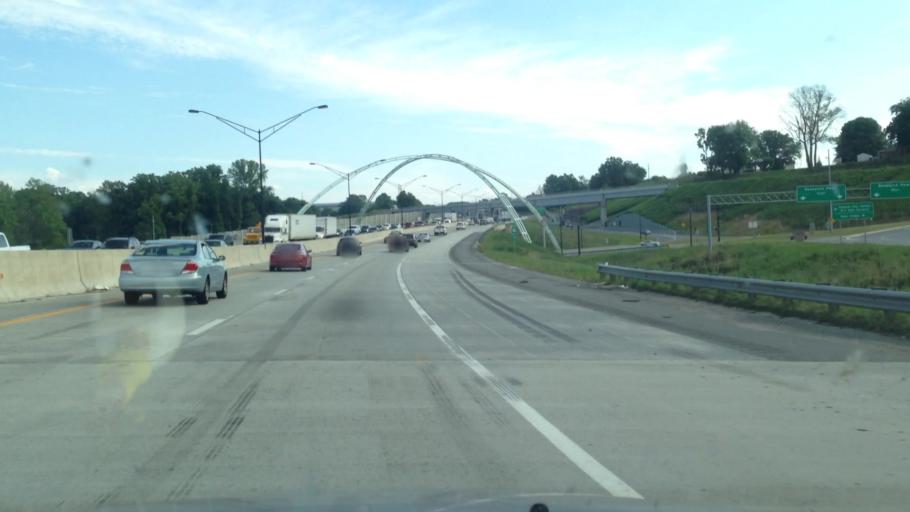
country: US
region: North Carolina
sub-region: Forsyth County
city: Winston-Salem
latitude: 36.0861
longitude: -80.2290
